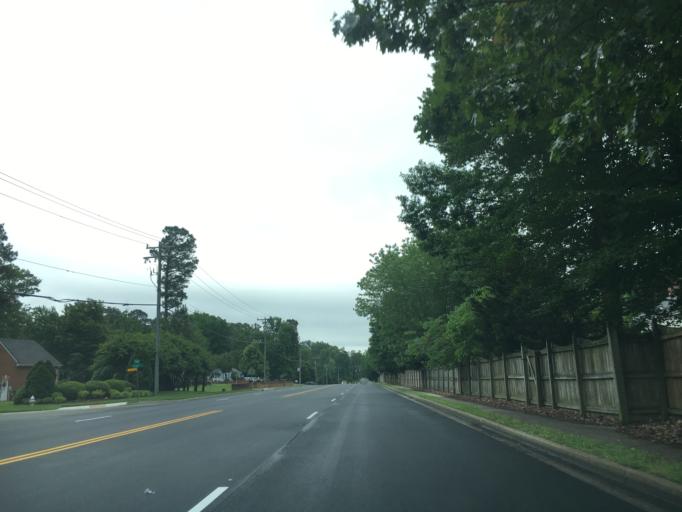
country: US
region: Virginia
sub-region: Henrico County
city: Short Pump
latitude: 37.6347
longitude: -77.6297
